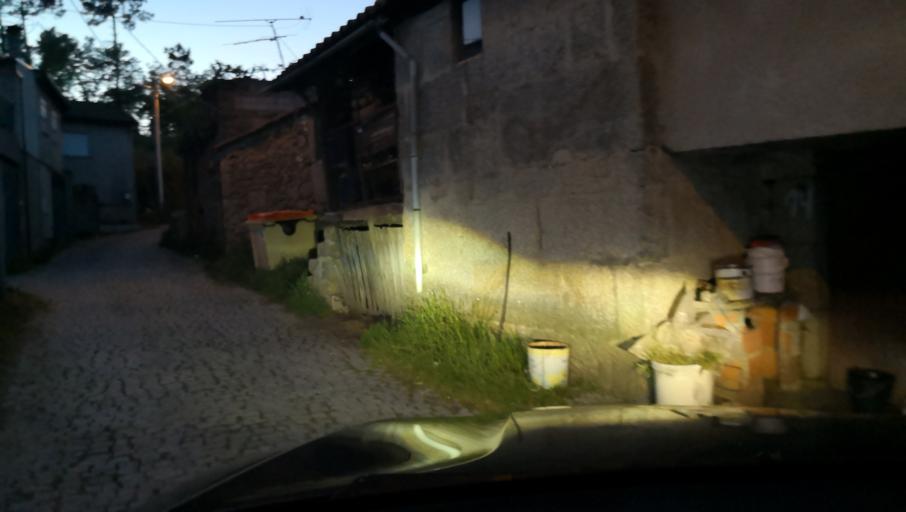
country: PT
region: Vila Real
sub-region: Vila Real
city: Vila Real
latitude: 41.3135
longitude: -7.6821
